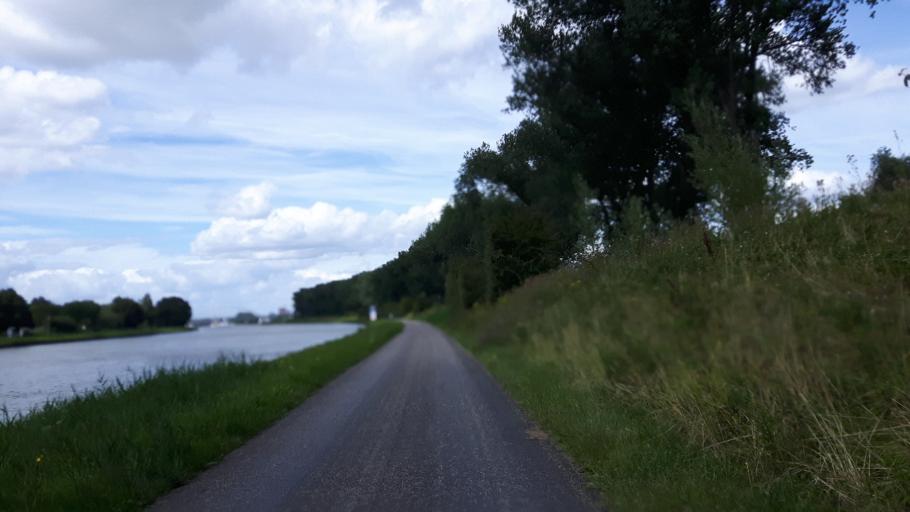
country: NL
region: Utrecht
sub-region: Gemeente Nieuwegein
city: Nieuwegein
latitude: 52.0260
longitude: 5.1153
